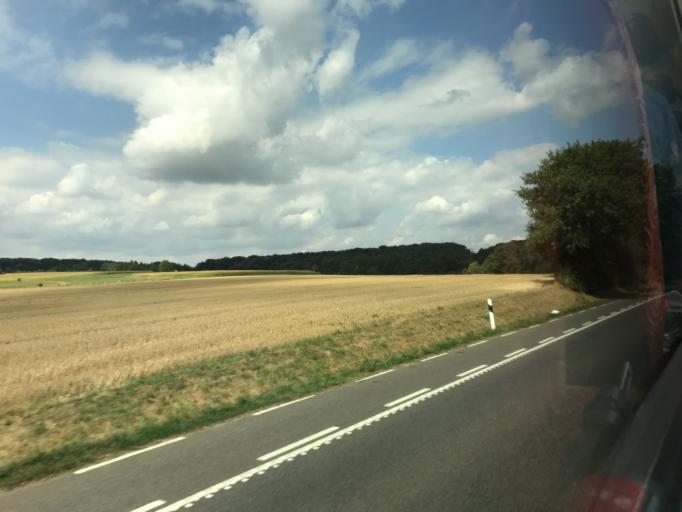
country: LU
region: Luxembourg
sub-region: Canton de Luxembourg
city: Weiler-la-Tour
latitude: 49.5363
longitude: 6.1782
